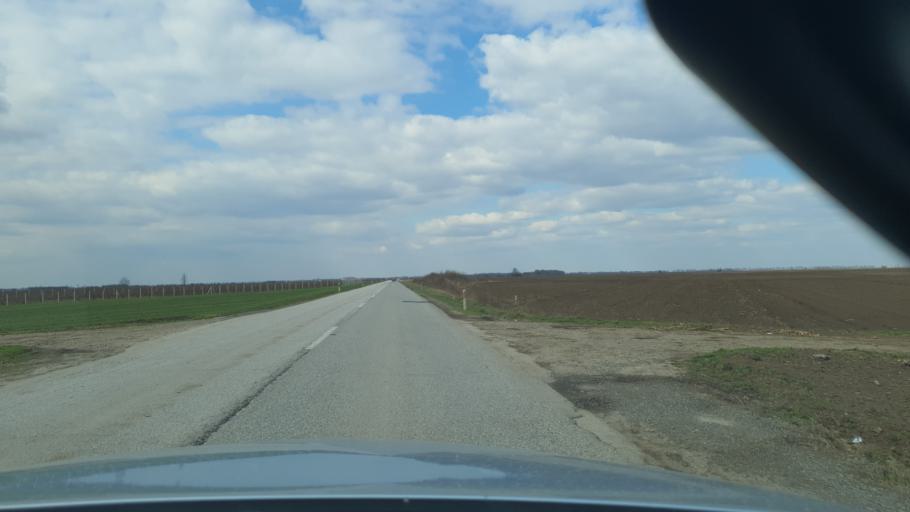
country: RS
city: Obrovac
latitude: 45.4224
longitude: 19.3946
